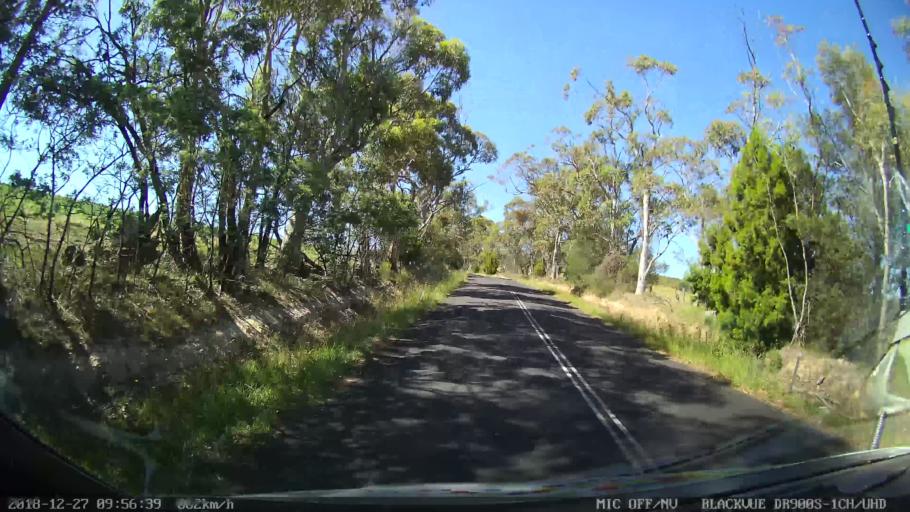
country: AU
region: New South Wales
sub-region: Lithgow
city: Portland
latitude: -33.4145
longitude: 149.9721
